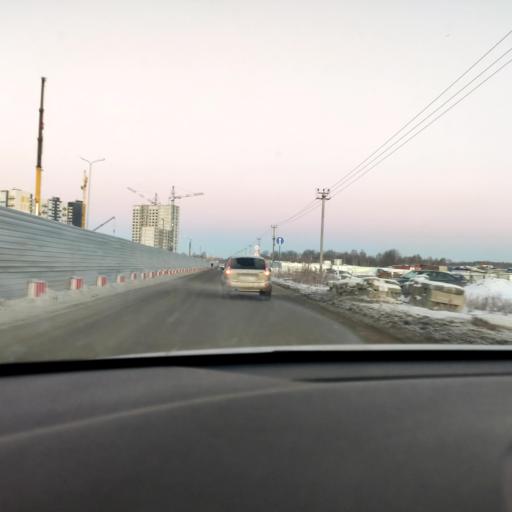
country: RU
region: Tatarstan
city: Osinovo
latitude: 55.8577
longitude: 48.9110
